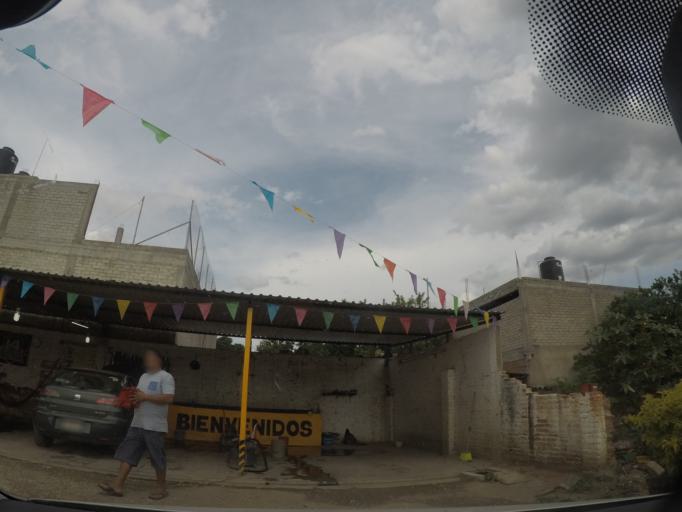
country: MX
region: Oaxaca
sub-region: Santa Cruz Amilpas
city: Santa Cruz Amilpas
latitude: 17.0623
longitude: -96.6818
